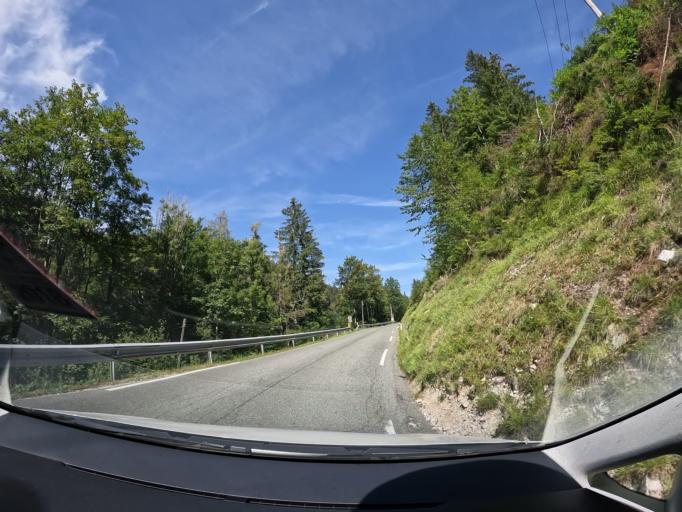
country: AT
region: Carinthia
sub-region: Politischer Bezirk Villach Land
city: Sankt Jakob
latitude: 46.5580
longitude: 14.0773
